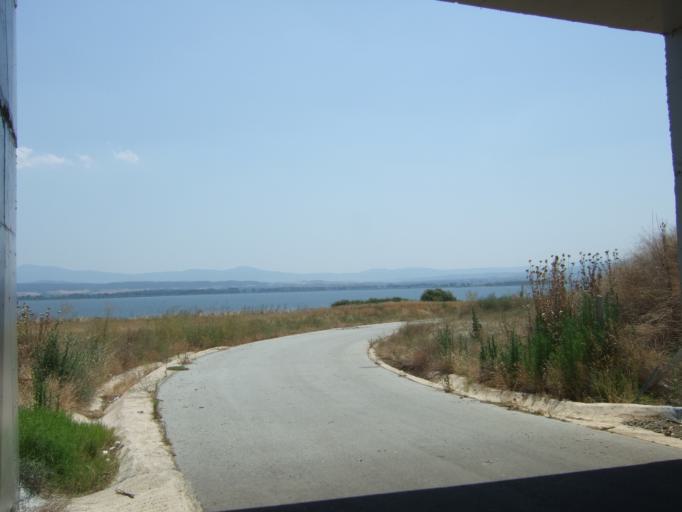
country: GR
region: Central Macedonia
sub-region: Nomos Thessalonikis
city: Nea Apollonia
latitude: 40.6935
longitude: 23.5027
